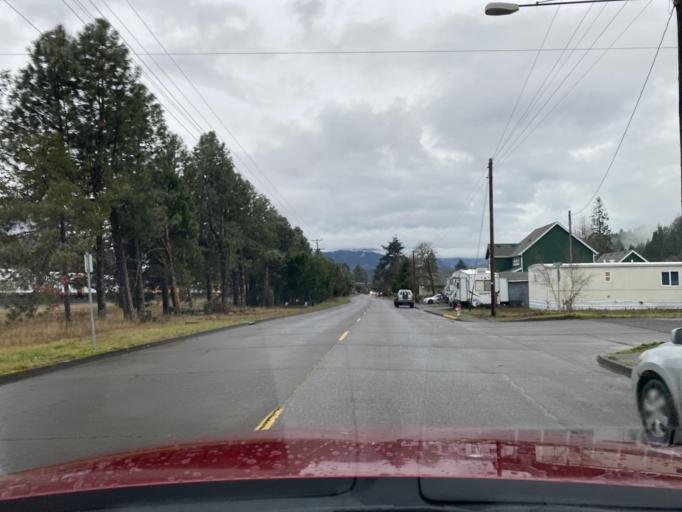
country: US
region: Oregon
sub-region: Lane County
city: Oakridge
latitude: 43.7470
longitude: -122.4620
